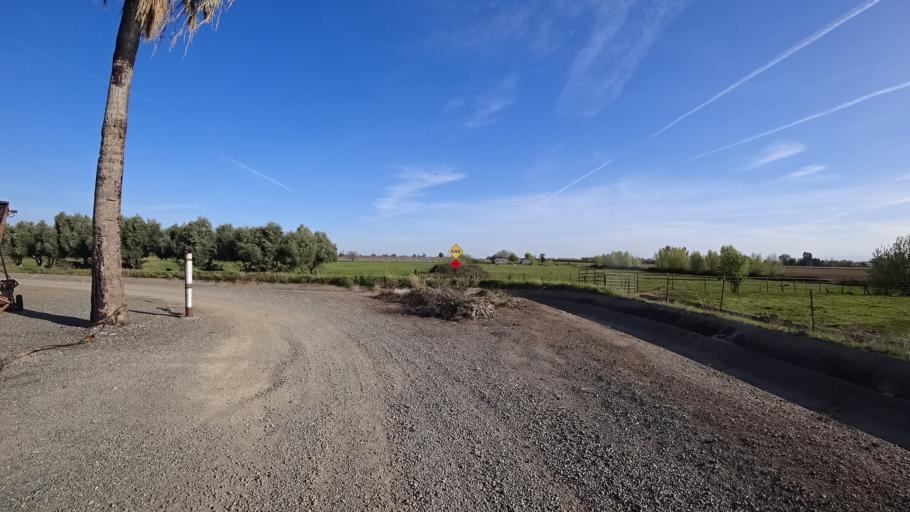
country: US
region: California
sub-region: Glenn County
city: Orland
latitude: 39.7332
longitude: -122.2343
